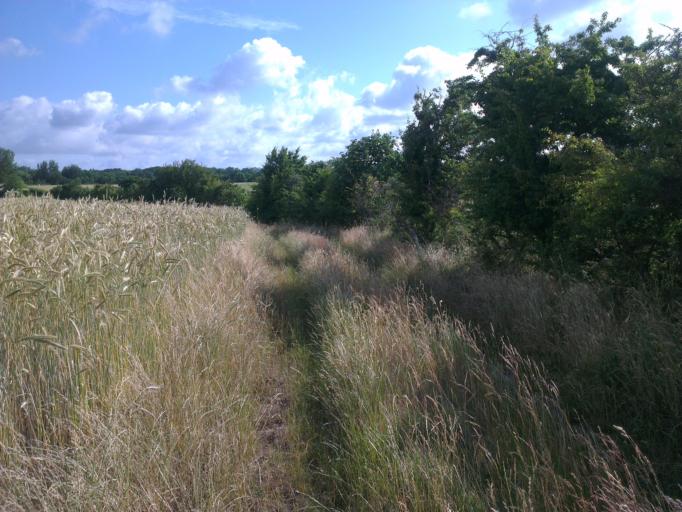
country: DK
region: Capital Region
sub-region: Frederikssund Kommune
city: Jaegerspris
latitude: 55.8755
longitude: 11.9780
